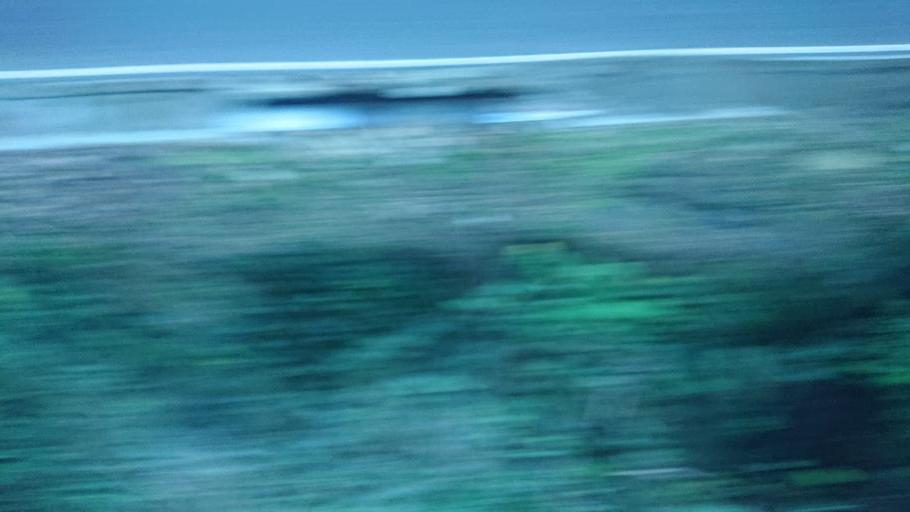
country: TW
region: Taiwan
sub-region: Chiayi
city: Jiayi Shi
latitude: 23.4746
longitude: 120.7192
